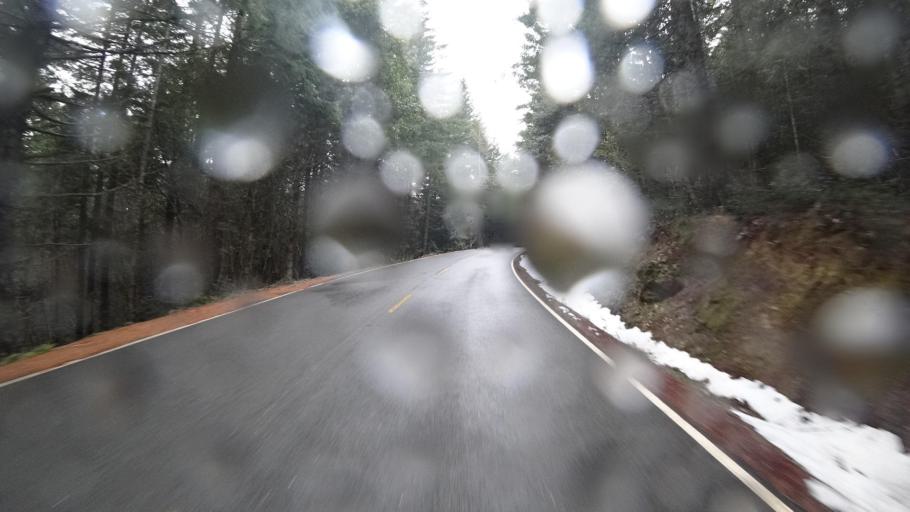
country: US
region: California
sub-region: Humboldt County
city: Willow Creek
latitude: 41.1544
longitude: -123.8182
